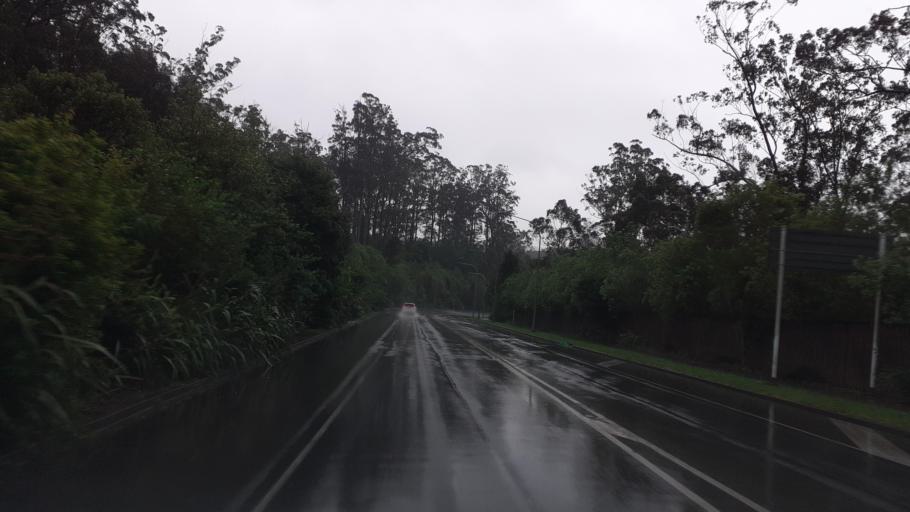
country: NZ
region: Northland
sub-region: Far North District
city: Kerikeri
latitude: -35.2210
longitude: 173.9526
